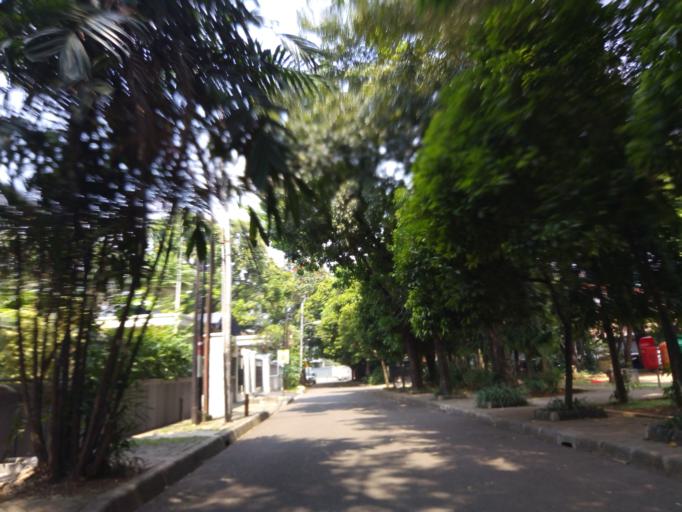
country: ID
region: Jakarta Raya
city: Jakarta
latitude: -6.2035
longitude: 106.8410
